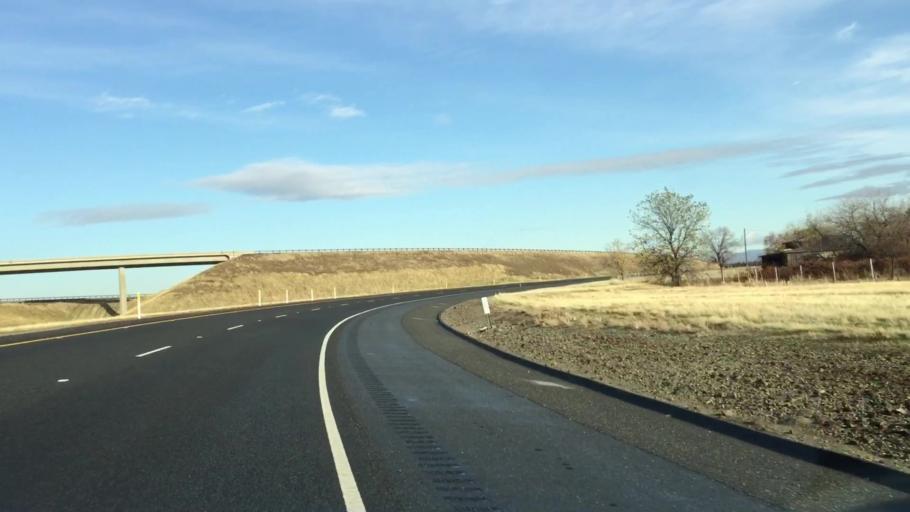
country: US
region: California
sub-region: Butte County
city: Thermalito
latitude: 39.5810
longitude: -121.6207
